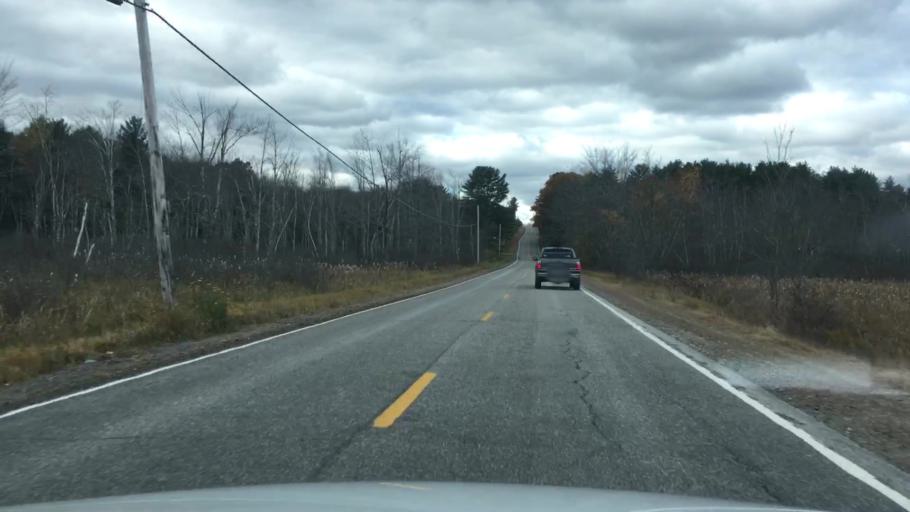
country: US
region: Maine
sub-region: Sagadahoc County
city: Richmond
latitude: 44.1074
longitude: -69.9006
